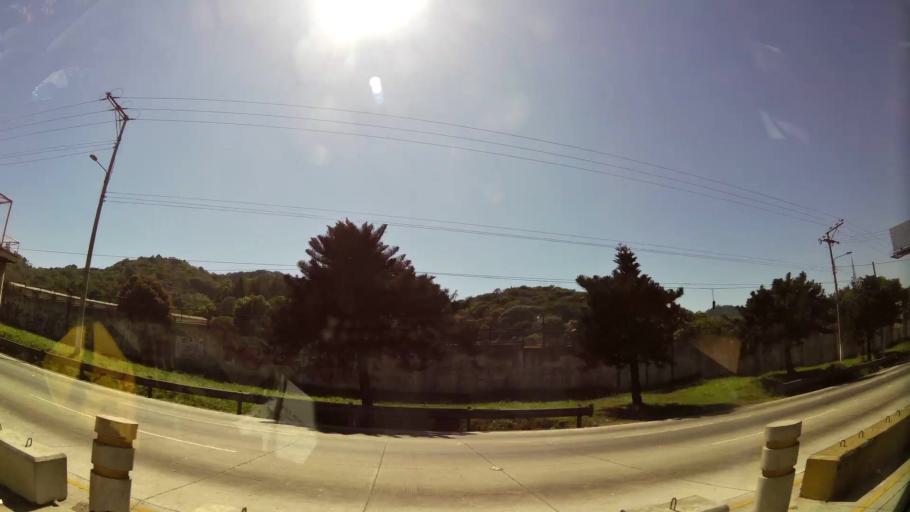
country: SV
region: La Libertad
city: Santa Tecla
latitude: 13.6748
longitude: -89.3025
